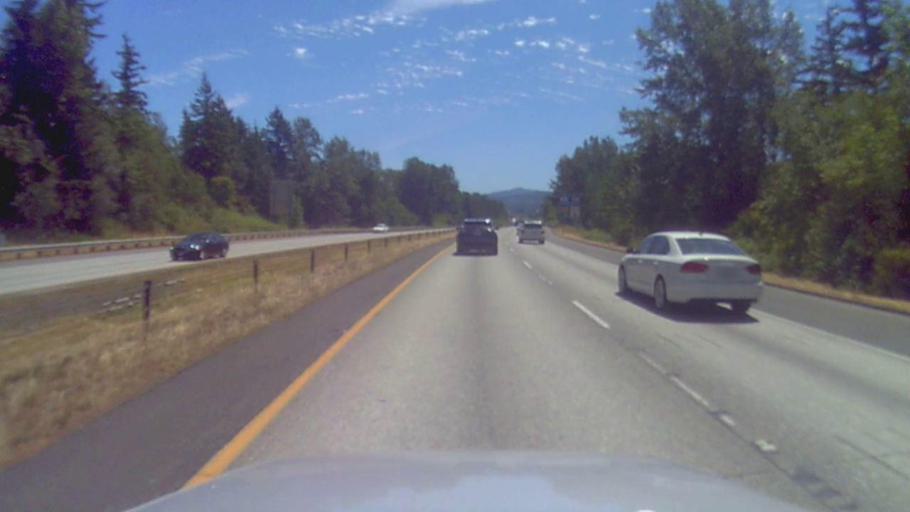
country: US
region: Washington
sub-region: Whatcom County
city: Bellingham
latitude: 48.7791
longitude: -122.4721
